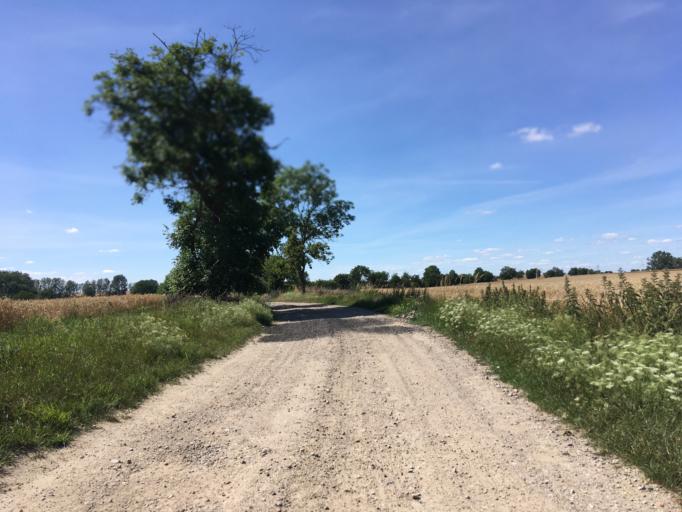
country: DE
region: Brandenburg
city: Brussow
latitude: 53.3249
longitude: 14.0925
